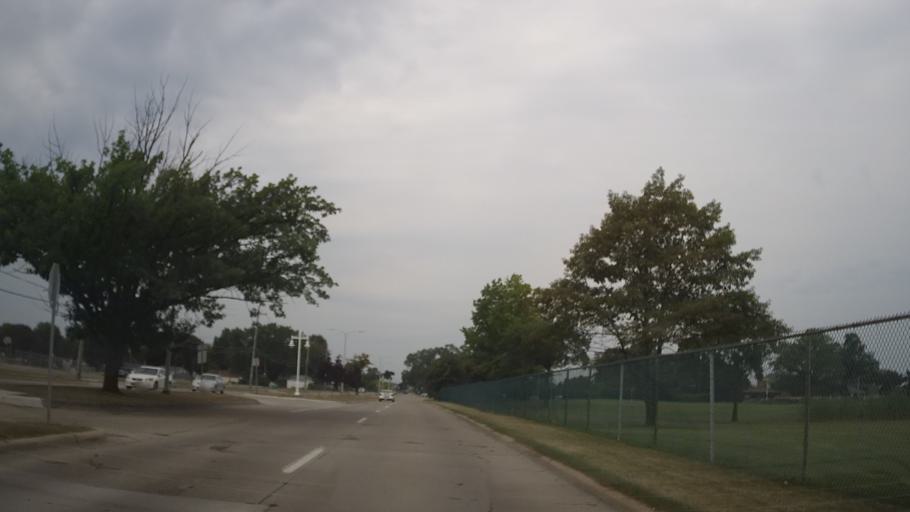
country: US
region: Michigan
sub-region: Macomb County
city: Saint Clair Shores
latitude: 42.5326
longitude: -82.8922
